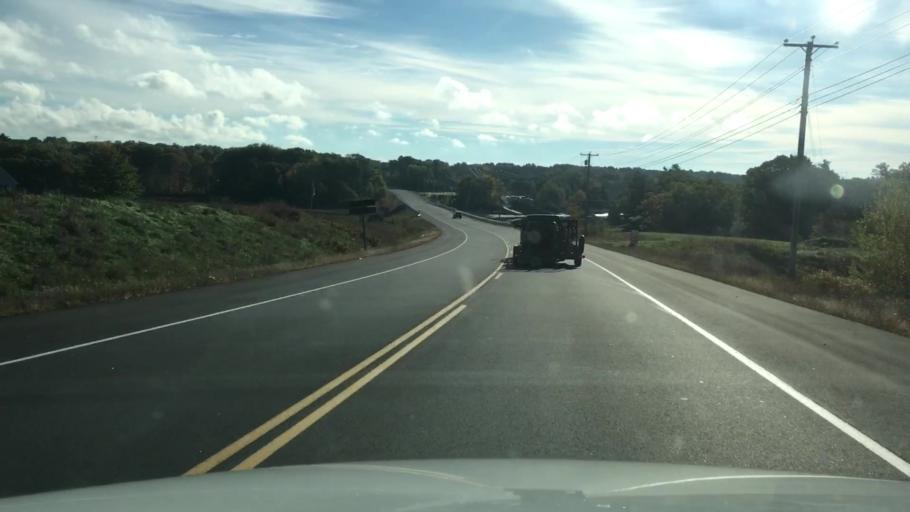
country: US
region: Maine
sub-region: Knox County
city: Thomaston
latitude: 44.0794
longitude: -69.2229
